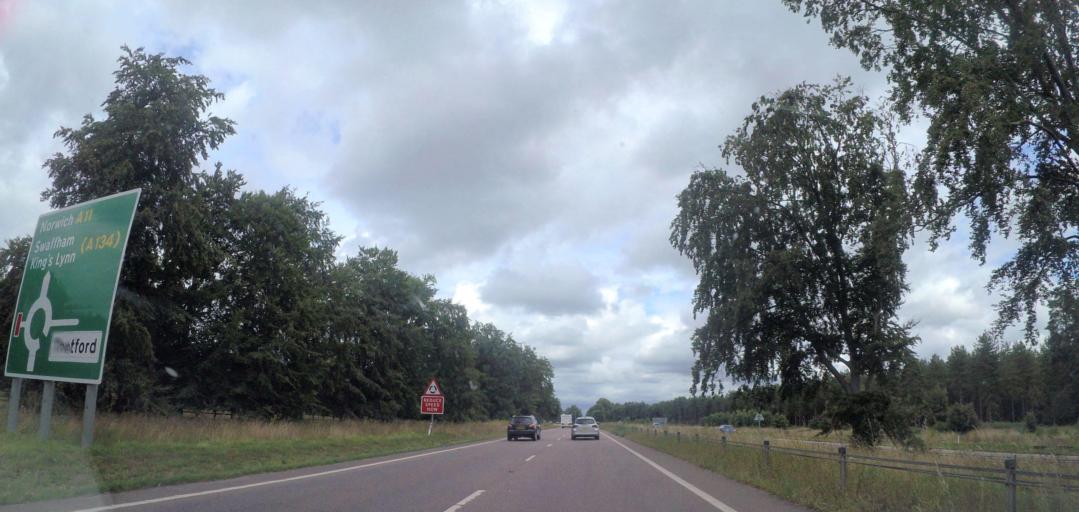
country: GB
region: England
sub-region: Norfolk
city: Thetford
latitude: 52.4004
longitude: 0.7123
